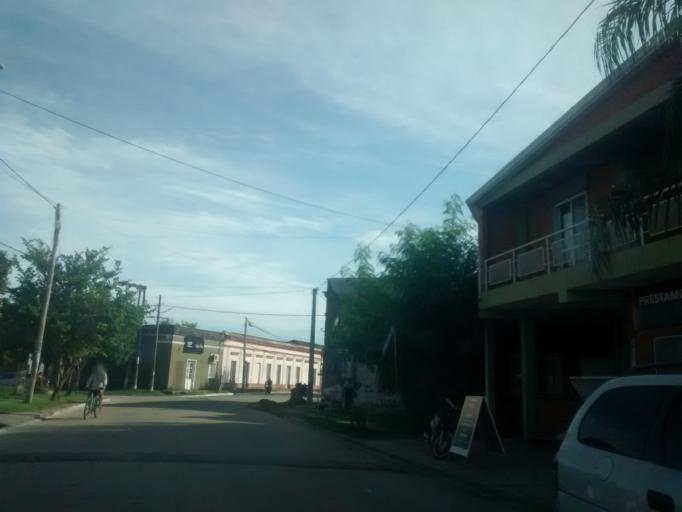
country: AR
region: Chaco
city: Puerto Tirol
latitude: -27.3726
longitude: -59.0910
